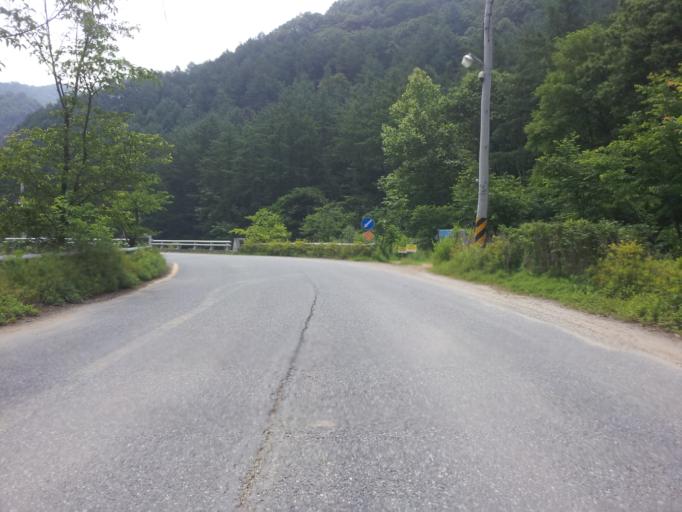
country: KR
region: Daejeon
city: Daejeon
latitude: 36.3321
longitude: 127.4911
